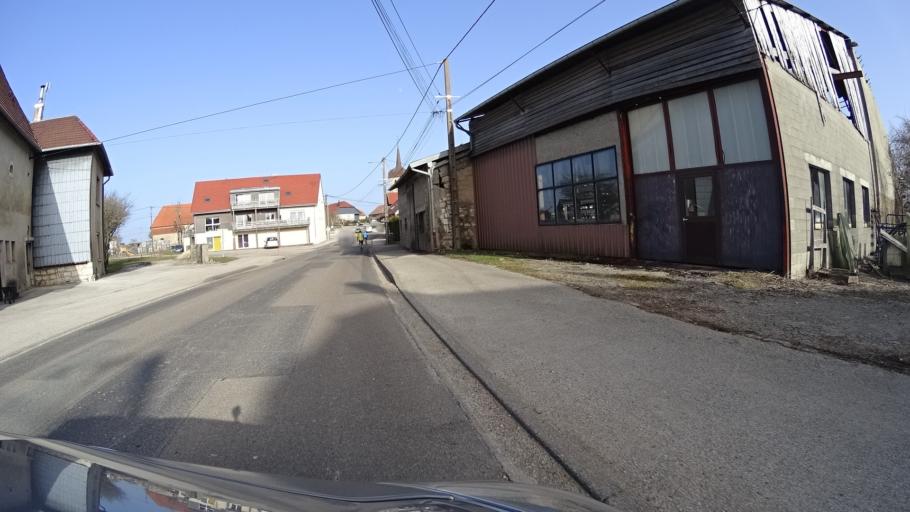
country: FR
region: Franche-Comte
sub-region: Departement du Doubs
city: Frasne
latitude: 46.8719
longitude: 6.1843
